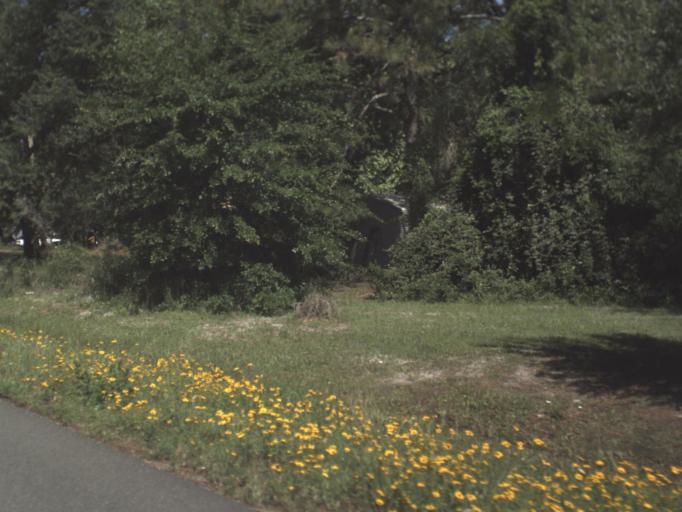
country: US
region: Florida
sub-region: Baker County
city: Macclenny
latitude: 30.2912
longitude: -82.0680
